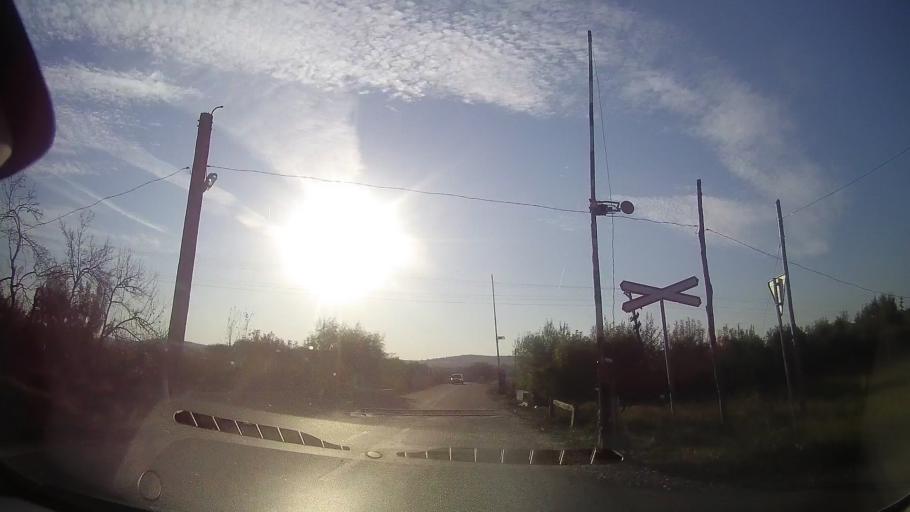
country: RO
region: Timis
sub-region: Comuna Masloc
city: Masloc
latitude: 45.9730
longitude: 21.4710
